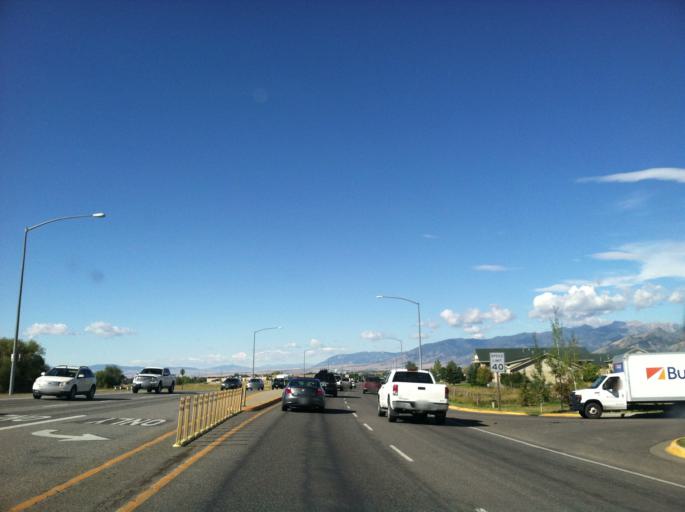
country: US
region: Montana
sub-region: Gallatin County
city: Bozeman
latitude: 45.7014
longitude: -111.0655
